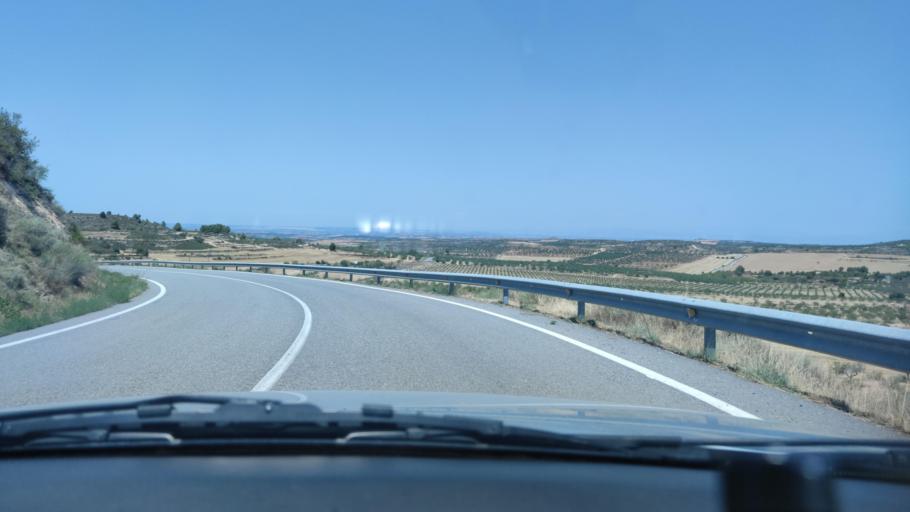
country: ES
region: Catalonia
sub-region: Provincia de Lleida
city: el Cogul
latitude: 41.4358
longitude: 0.6481
